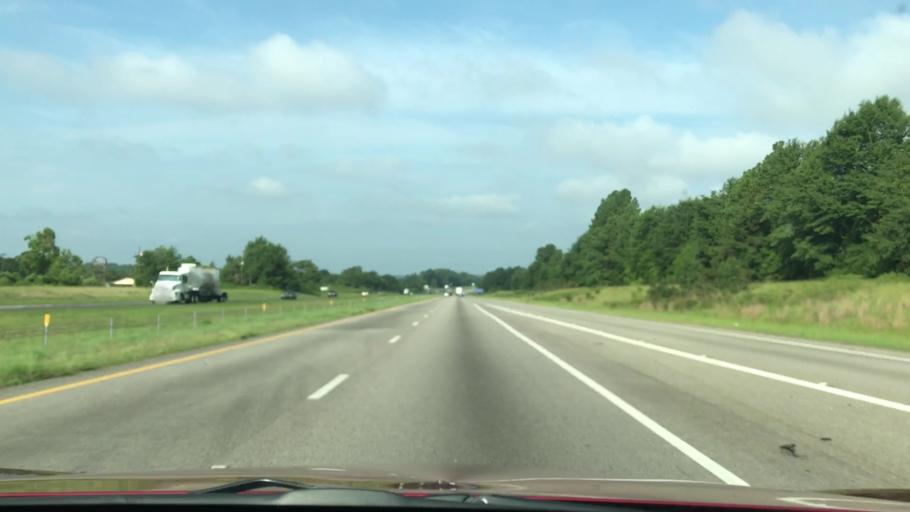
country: US
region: South Carolina
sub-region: Aiken County
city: Aiken
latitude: 33.6644
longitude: -81.6787
